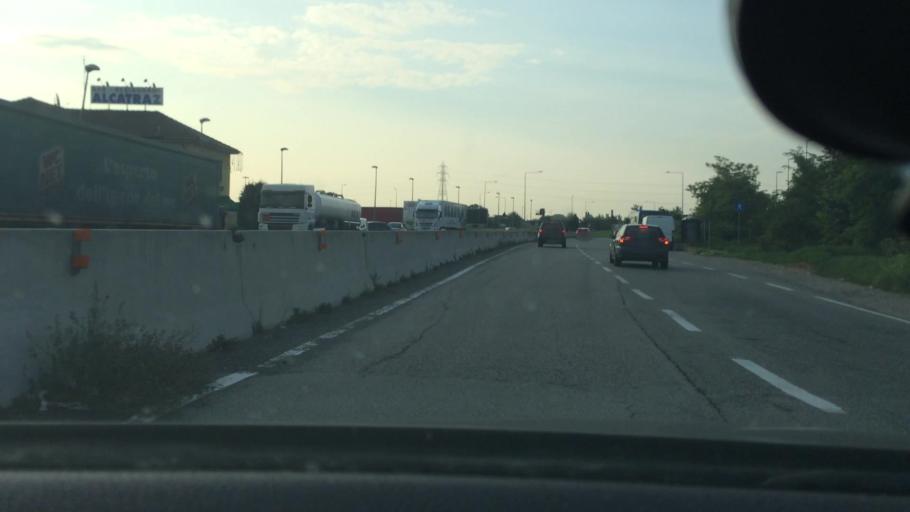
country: IT
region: Lombardy
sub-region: Citta metropolitana di Milano
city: Santo Stefano Ticino
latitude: 45.5018
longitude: 8.9184
